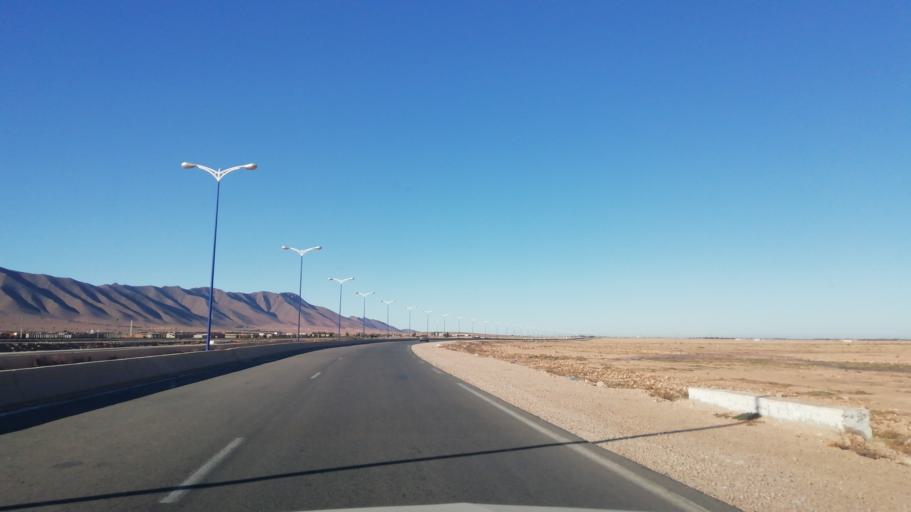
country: DZ
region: Wilaya de Naama
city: Naama
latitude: 33.5672
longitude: -0.2402
